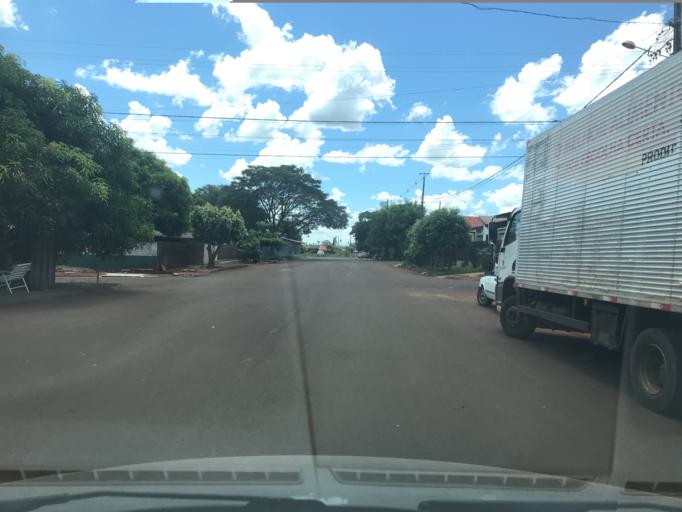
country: BR
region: Parana
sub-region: Palotina
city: Palotina
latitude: -24.2699
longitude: -53.8475
